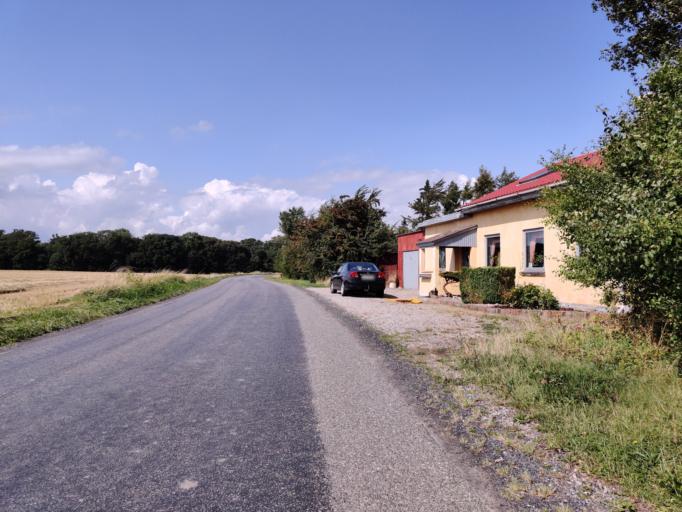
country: DK
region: Zealand
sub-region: Guldborgsund Kommune
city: Nykobing Falster
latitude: 54.6409
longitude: 11.8964
